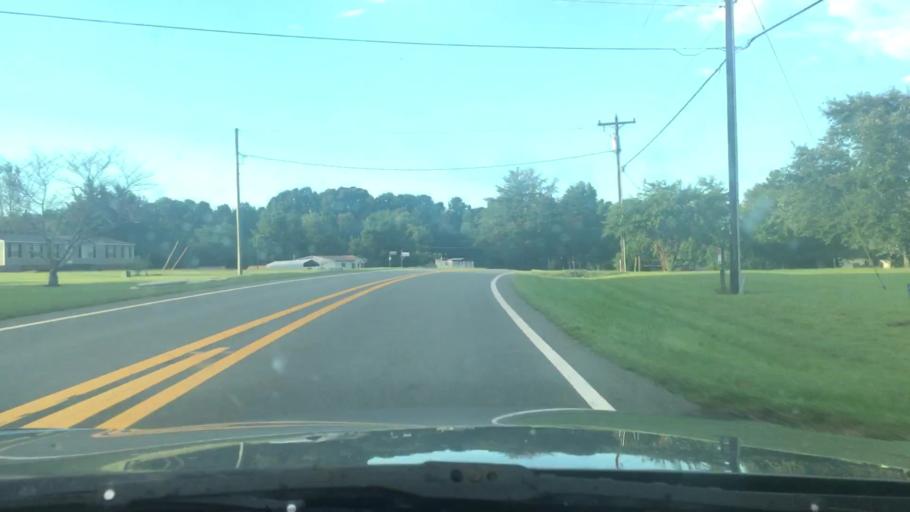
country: US
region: North Carolina
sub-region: Alamance County
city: Green Level
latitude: 36.1988
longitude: -79.3228
